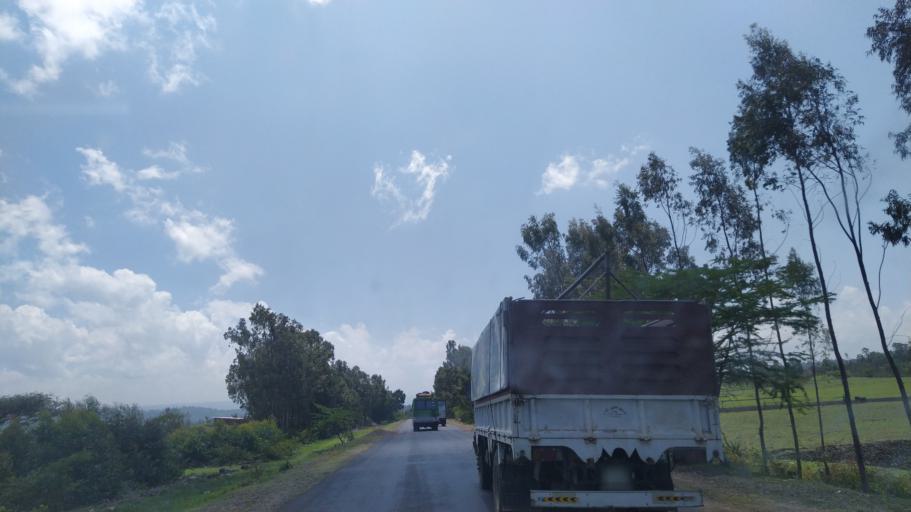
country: ET
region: Southern Nations, Nationalities, and People's Region
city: Butajira
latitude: 7.7686
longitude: 38.1373
